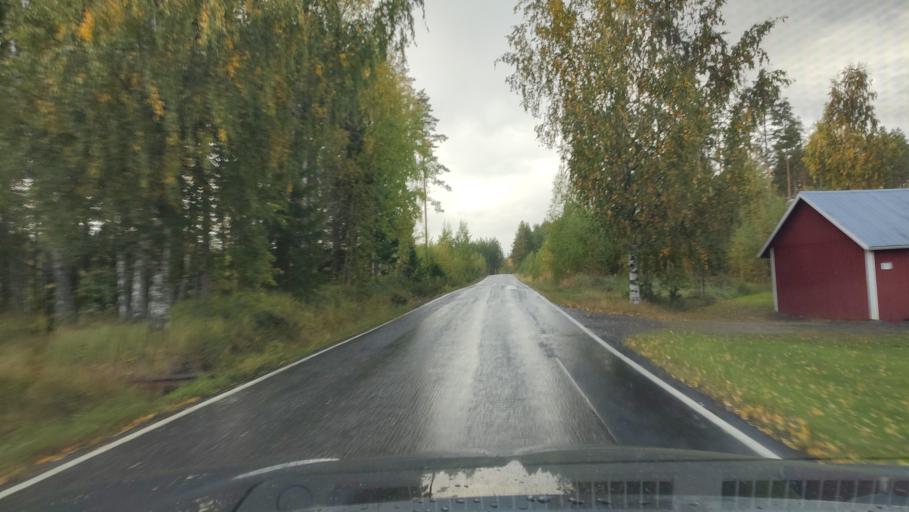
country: FI
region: Southern Ostrobothnia
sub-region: Suupohja
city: Karijoki
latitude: 62.3174
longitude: 21.6837
